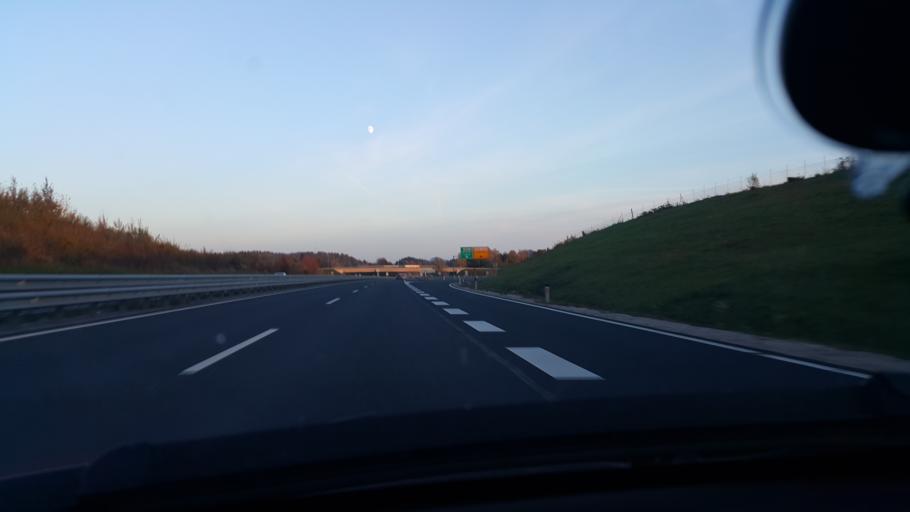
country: SI
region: Zalec
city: Zalec
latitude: 46.2644
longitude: 15.2132
